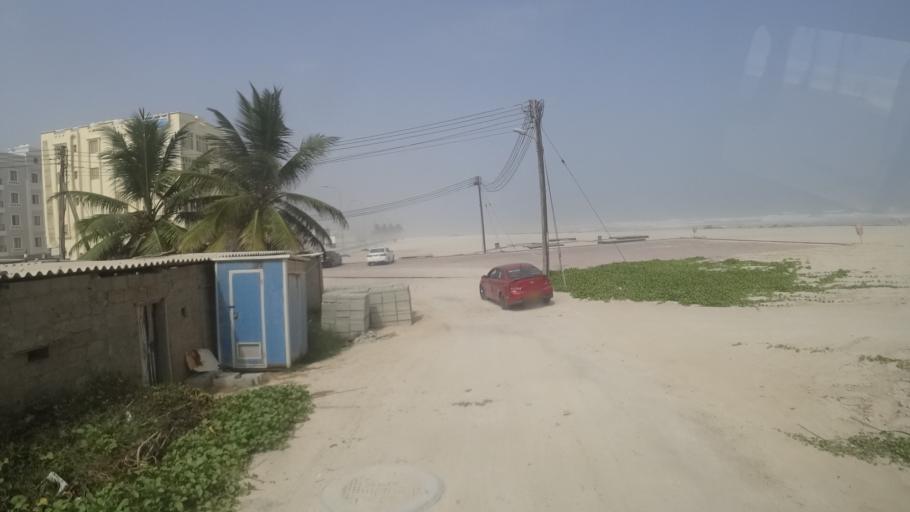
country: OM
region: Zufar
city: Salalah
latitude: 17.0098
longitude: 54.1629
